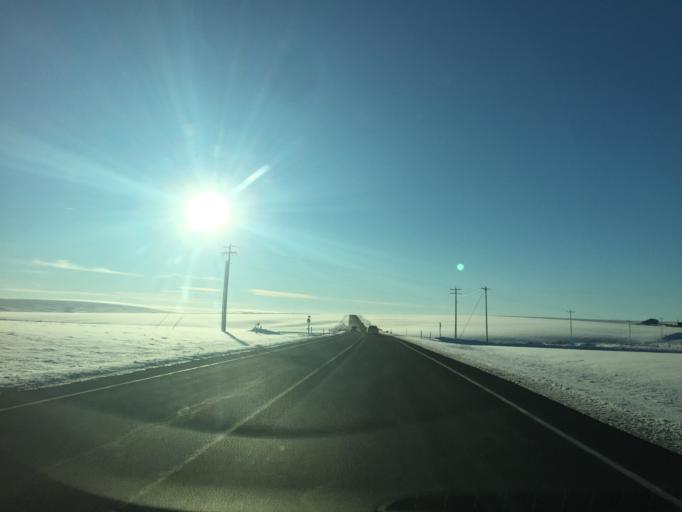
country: US
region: Washington
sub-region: Okanogan County
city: Coulee Dam
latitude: 47.6998
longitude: -118.9563
